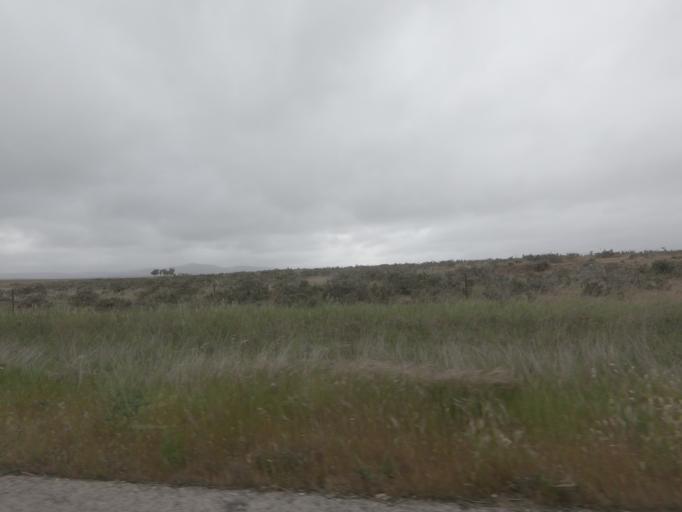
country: ES
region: Extremadura
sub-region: Provincia de Caceres
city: Malpartida de Caceres
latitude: 39.3544
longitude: -6.4673
